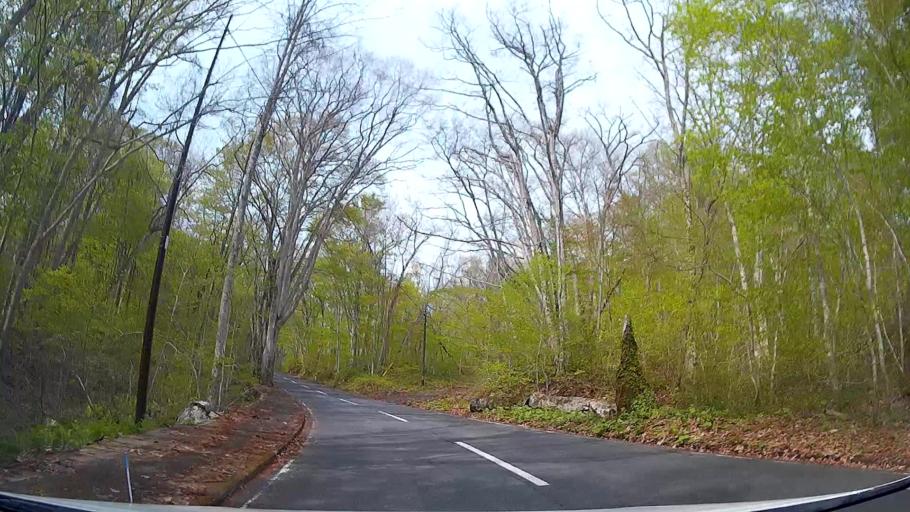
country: JP
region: Akita
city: Hanawa
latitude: 40.4322
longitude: 140.9154
